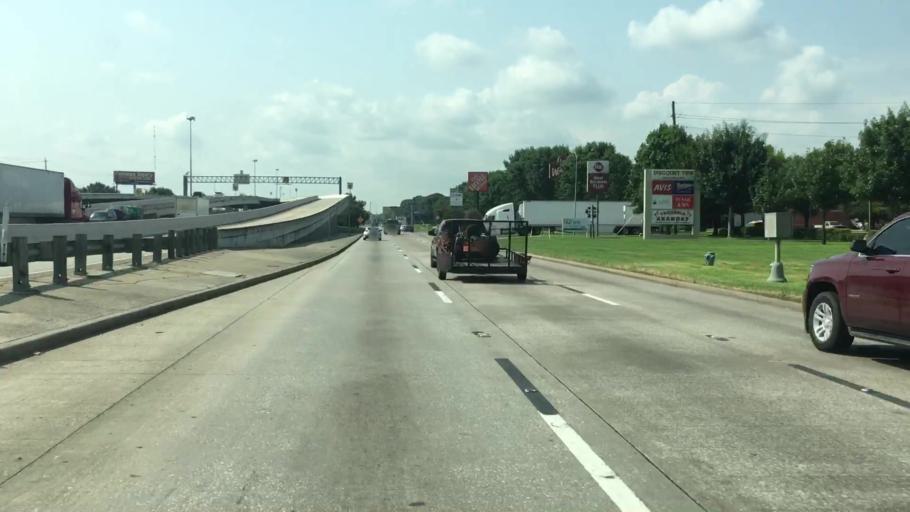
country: US
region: Texas
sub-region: Harris County
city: Aldine
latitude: 29.9221
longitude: -95.4127
